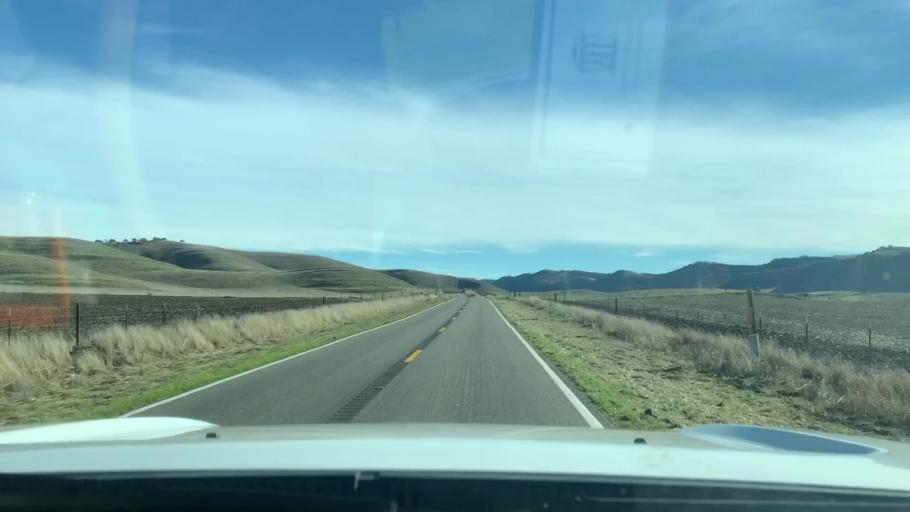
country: US
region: California
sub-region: Monterey County
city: King City
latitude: 36.1658
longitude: -120.8781
